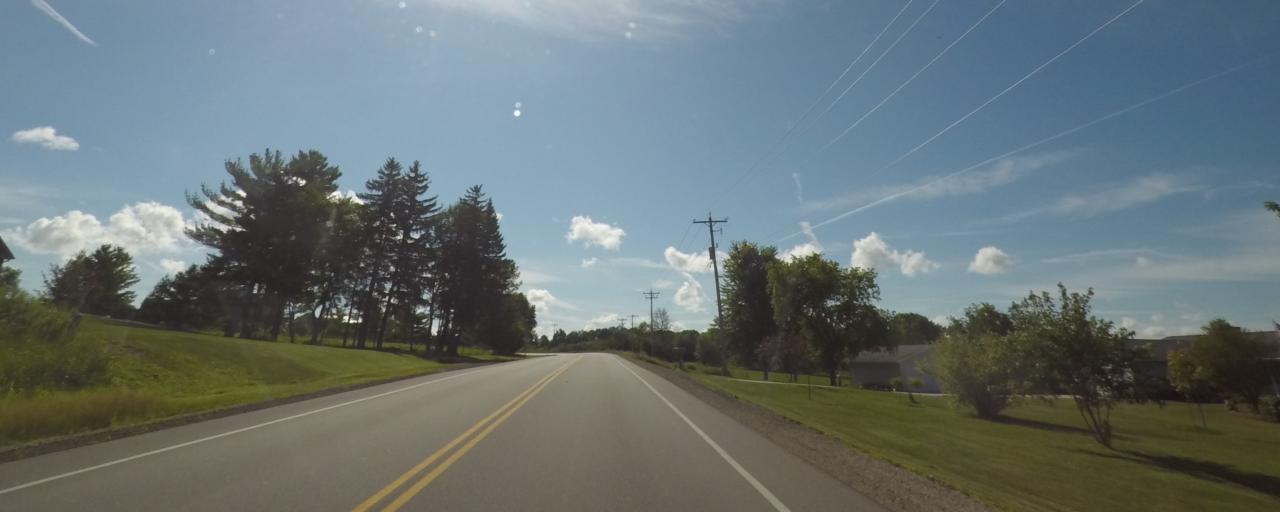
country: US
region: Wisconsin
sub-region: Jefferson County
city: Ixonia
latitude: 43.0687
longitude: -88.6319
